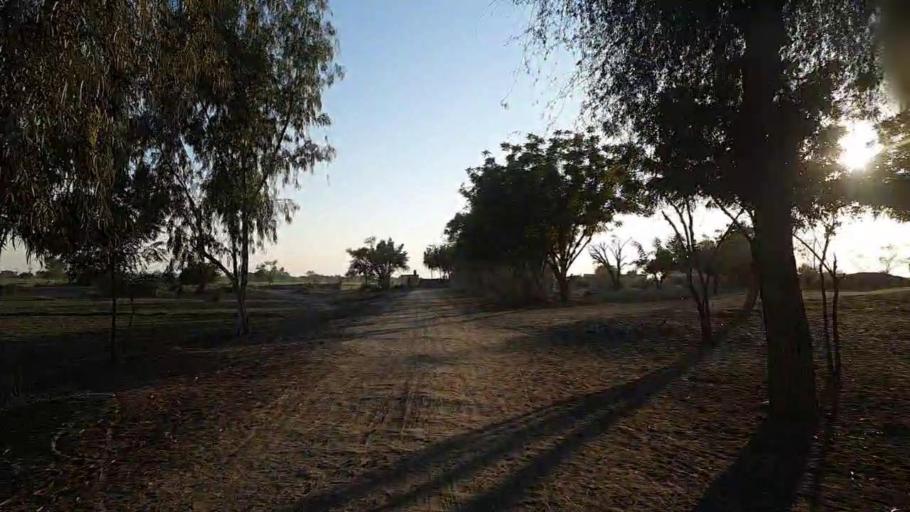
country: PK
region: Sindh
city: Khairpur
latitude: 27.9089
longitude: 69.6808
